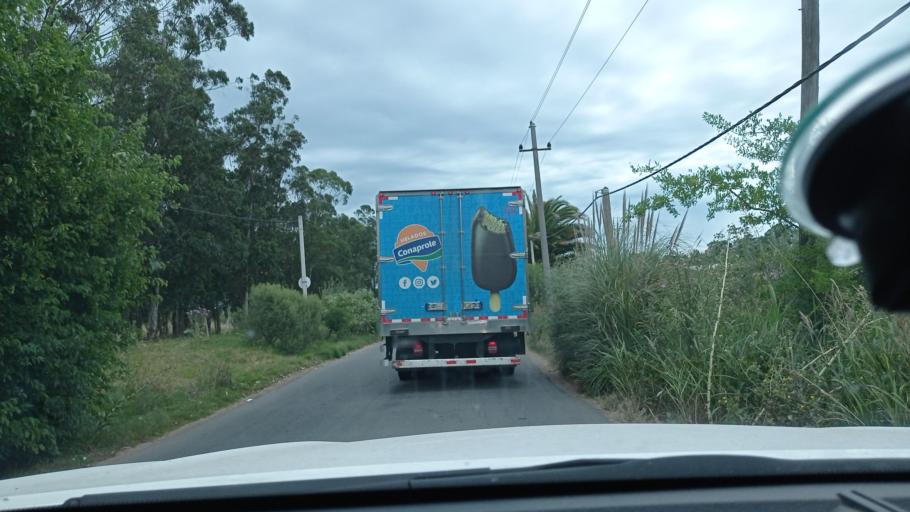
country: UY
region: Canelones
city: La Paz
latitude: -34.8072
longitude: -56.1890
